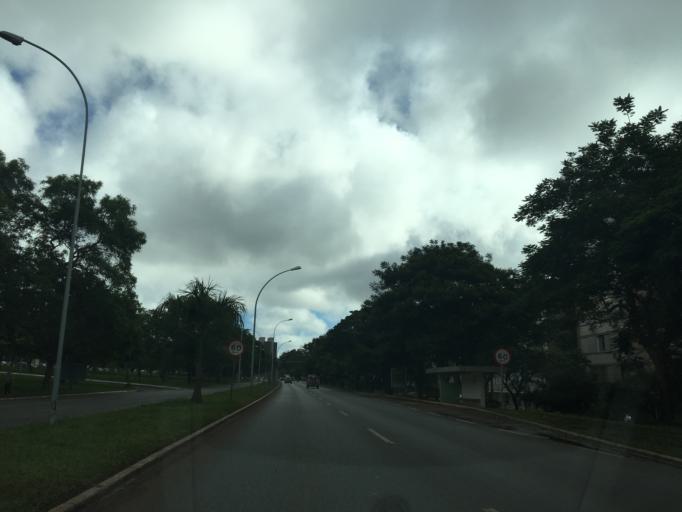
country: BR
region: Federal District
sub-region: Brasilia
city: Brasilia
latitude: -15.8132
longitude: -47.8951
